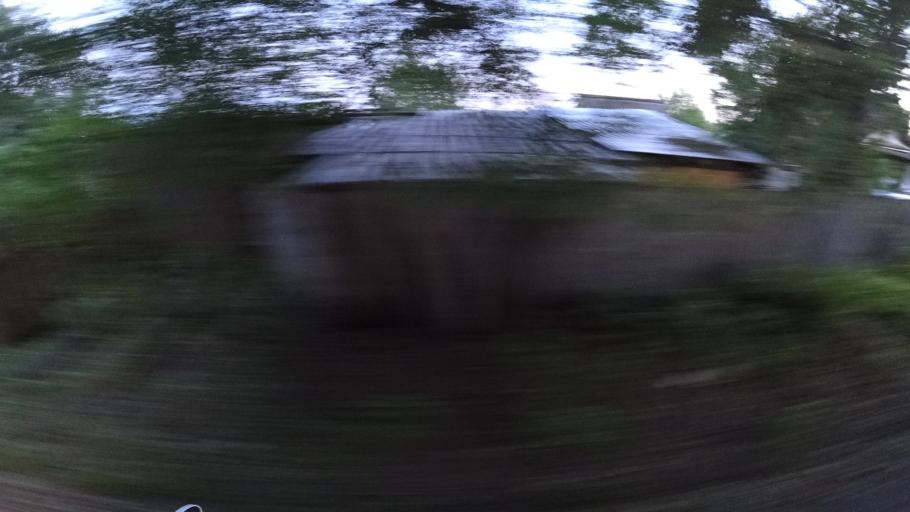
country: RU
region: Khabarovsk Krai
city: Khor
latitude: 47.8572
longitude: 134.9438
